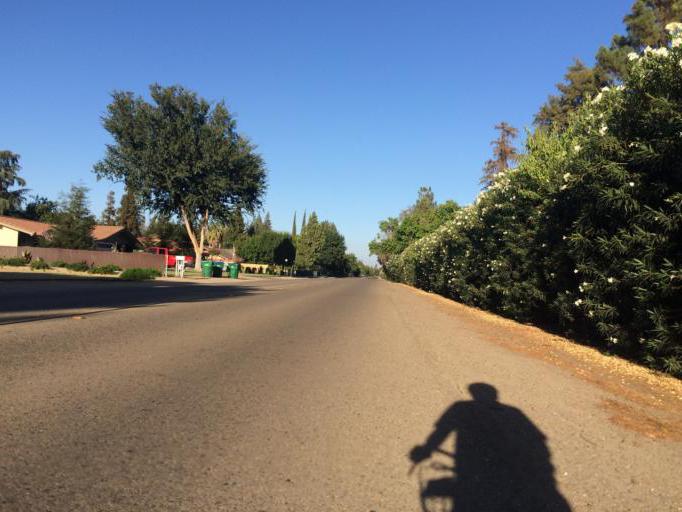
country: US
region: California
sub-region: Fresno County
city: Sunnyside
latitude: 36.7291
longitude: -119.6908
